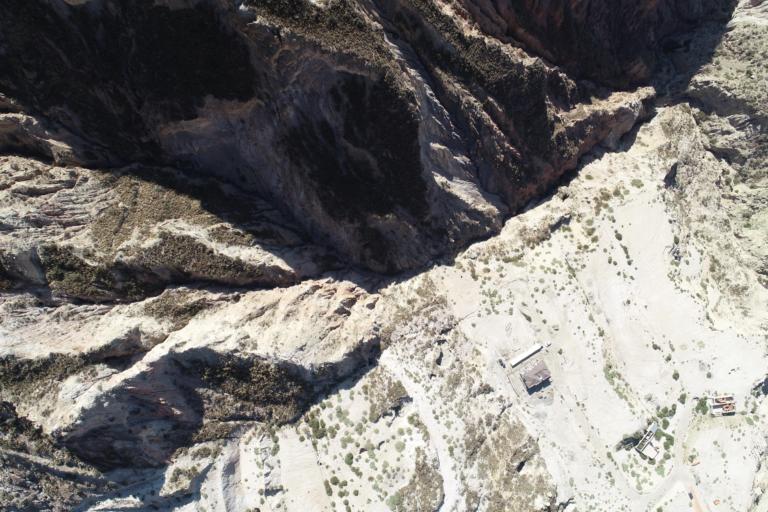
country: BO
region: La Paz
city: La Paz
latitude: -16.5543
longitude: -68.1060
